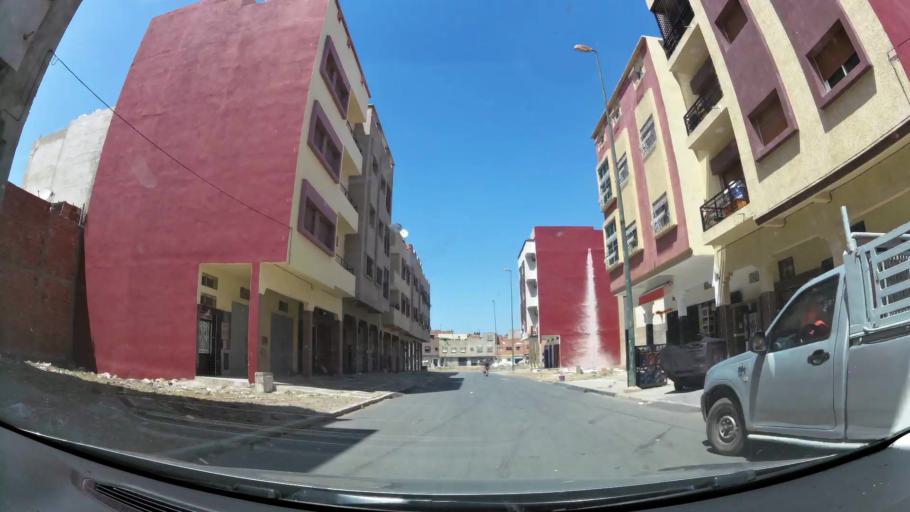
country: MA
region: Gharb-Chrarda-Beni Hssen
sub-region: Kenitra Province
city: Kenitra
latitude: 34.2450
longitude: -6.5376
